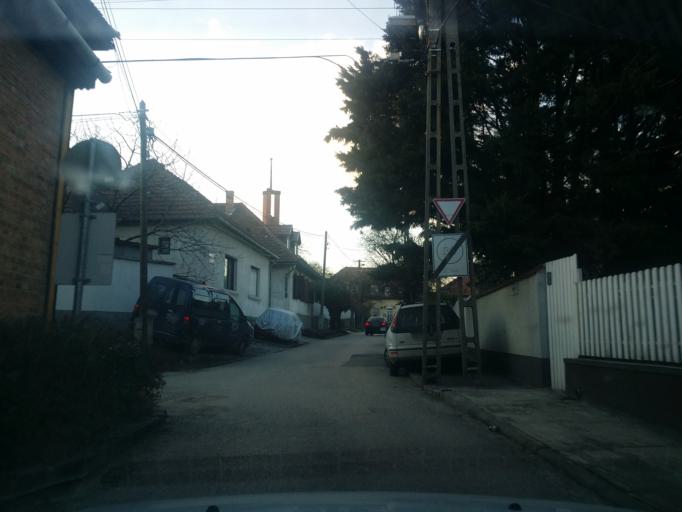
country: HU
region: Pest
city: Pilisvorosvar
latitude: 47.6187
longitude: 18.9167
